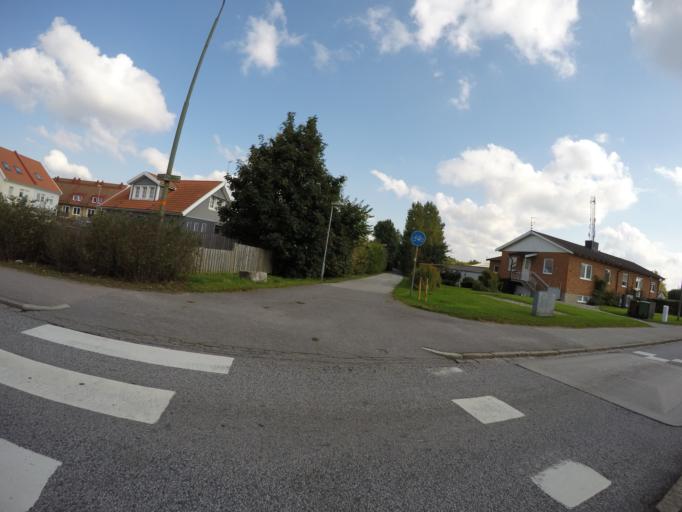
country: SE
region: Skane
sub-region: Burlovs Kommun
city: Arloev
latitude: 55.5863
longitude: 13.0859
